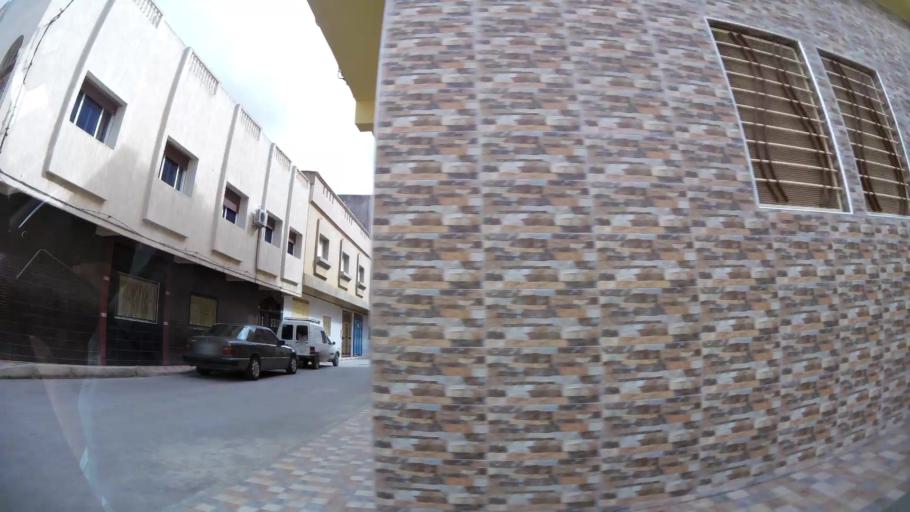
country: MA
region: Oriental
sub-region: Nador
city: Nador
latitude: 35.1609
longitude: -2.9371
